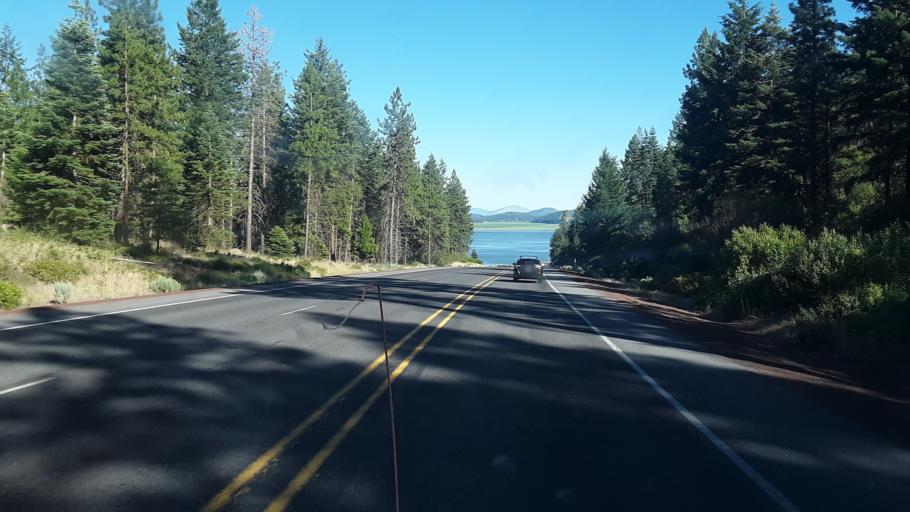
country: US
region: Oregon
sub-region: Klamath County
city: Klamath Falls
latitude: 42.3255
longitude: -121.9497
